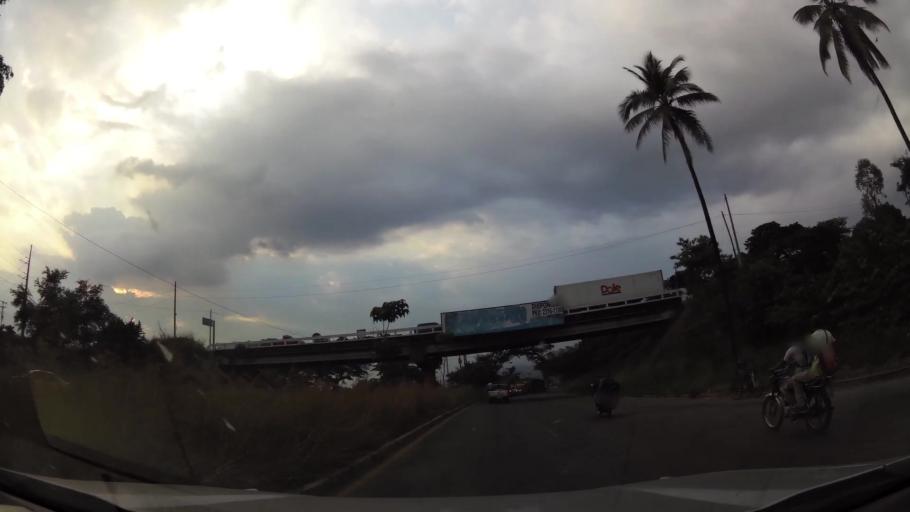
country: GT
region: Escuintla
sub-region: Municipio de Escuintla
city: Escuintla
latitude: 14.2823
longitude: -90.7871
